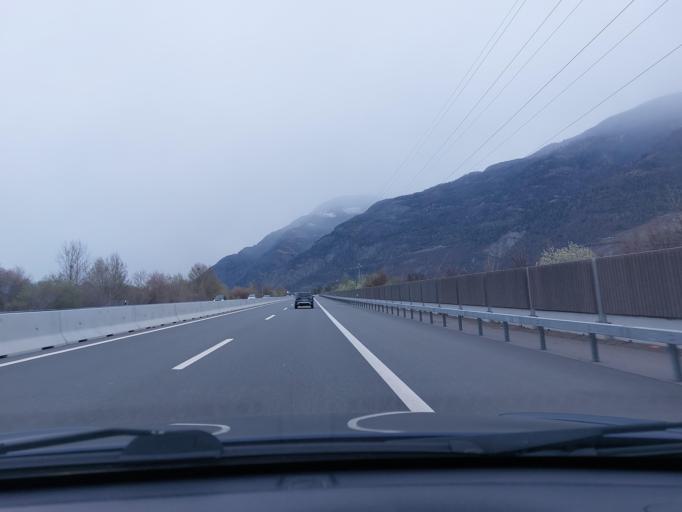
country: CH
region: Valais
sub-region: Martigny District
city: Saxon
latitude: 46.1574
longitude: 7.1769
